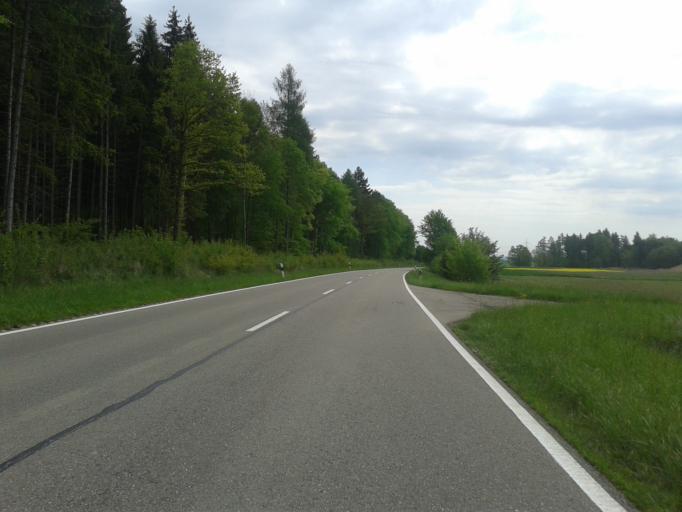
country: DE
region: Baden-Wuerttemberg
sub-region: Tuebingen Region
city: Erbach
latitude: 48.3543
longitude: 9.8516
